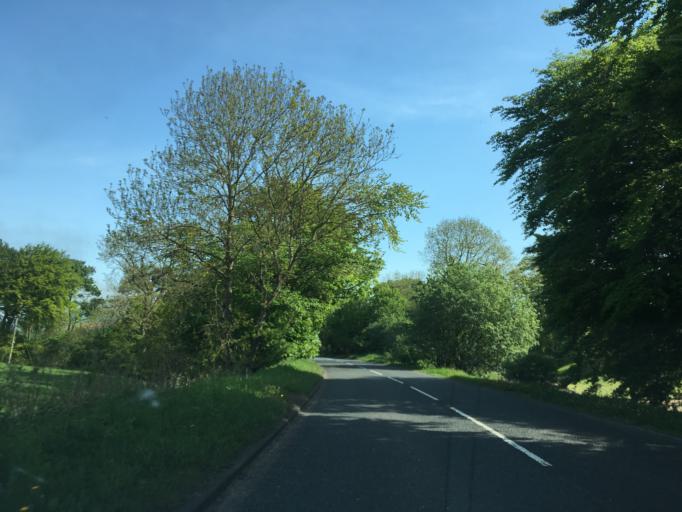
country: GB
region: Scotland
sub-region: The Scottish Borders
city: West Linton
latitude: 55.6790
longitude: -3.4032
